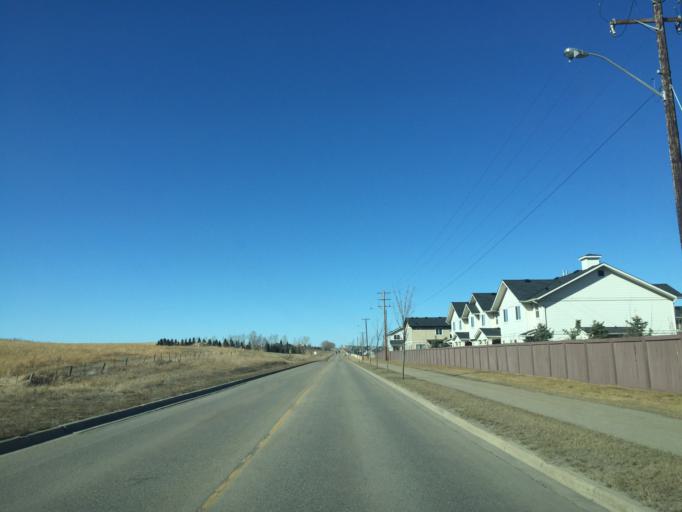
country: CA
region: Alberta
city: Airdrie
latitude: 51.2912
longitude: -114.0485
